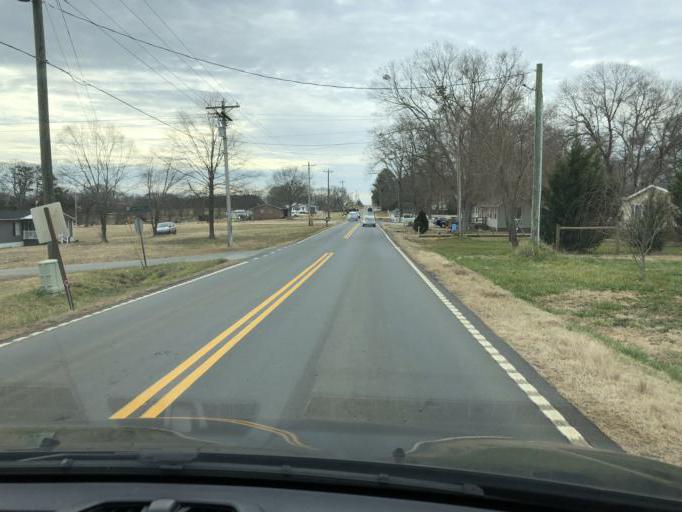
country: US
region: South Carolina
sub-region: Greenville County
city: Five Forks
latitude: 34.8531
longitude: -82.1938
